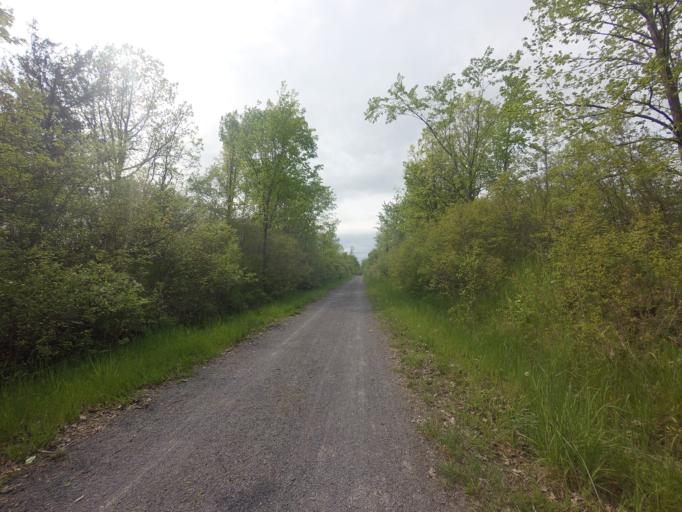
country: CA
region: Ontario
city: Kingston
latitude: 44.3513
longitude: -76.6153
